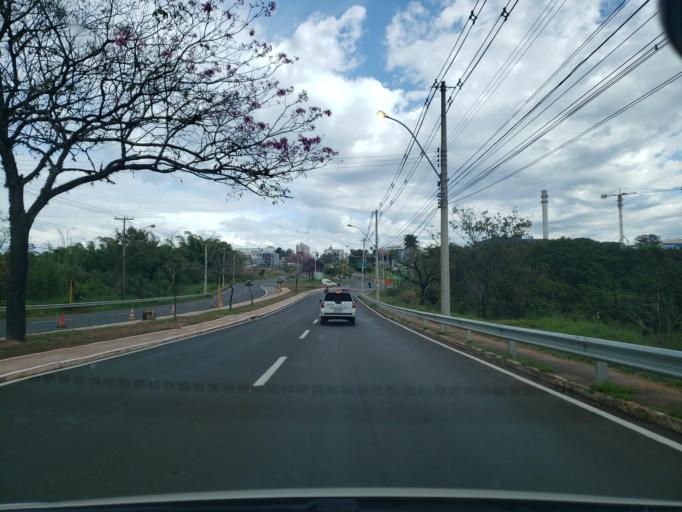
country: BR
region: Sao Paulo
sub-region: Bauru
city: Bauru
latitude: -22.3373
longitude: -49.0393
